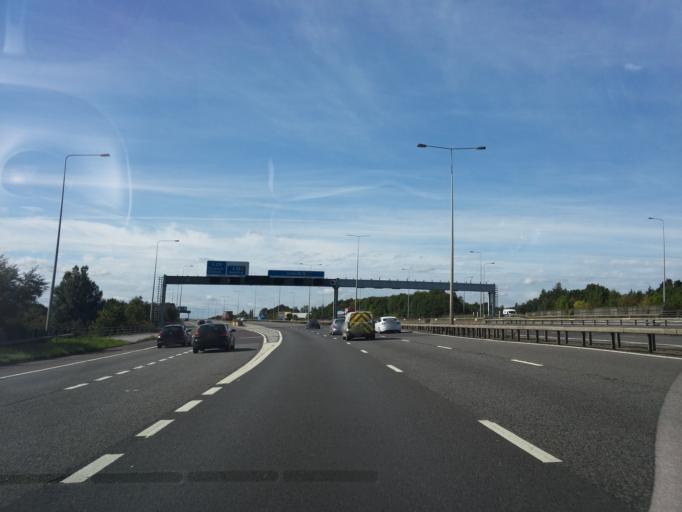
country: GB
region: England
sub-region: Kent
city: Boxley
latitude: 51.2988
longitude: 0.5199
